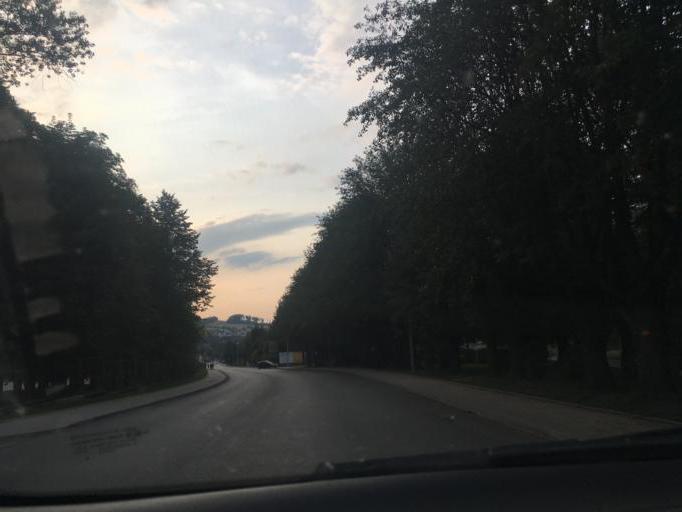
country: PL
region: Lower Silesian Voivodeship
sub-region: Powiat klodzki
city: Bozkow
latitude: 50.5406
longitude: 16.5613
